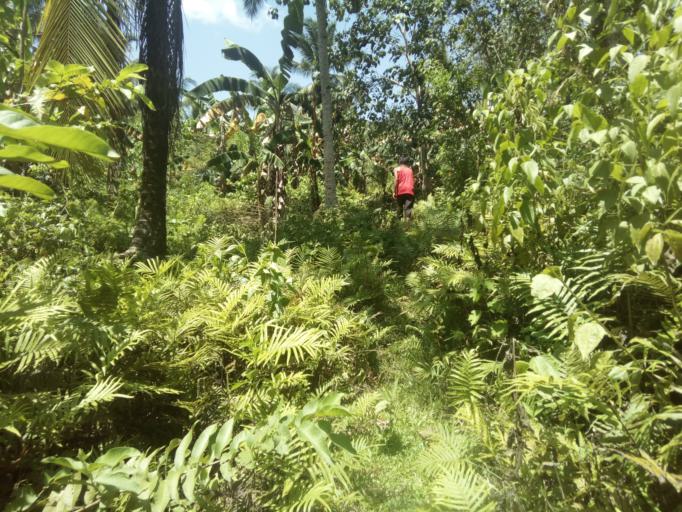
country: PH
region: Caraga
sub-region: Province of Agusan del Sur
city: Santa Josefa
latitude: 7.9586
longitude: 125.9885
